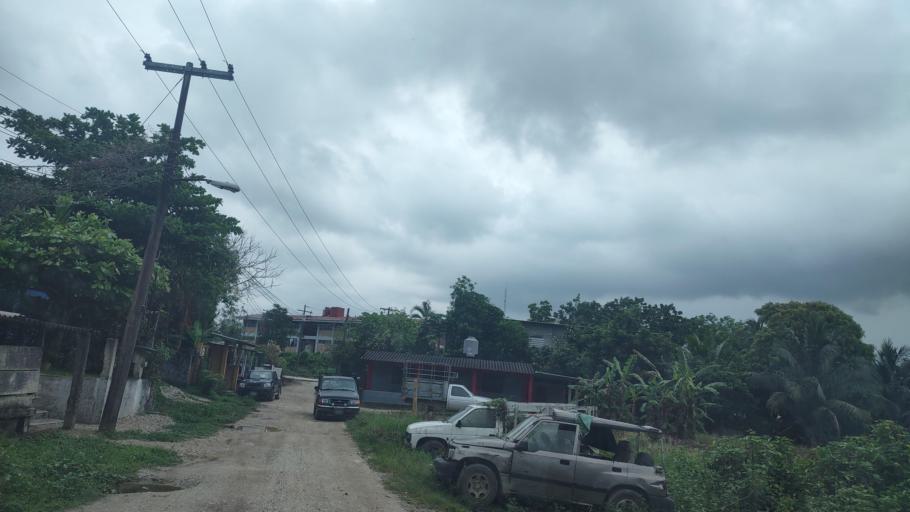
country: MX
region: Veracruz
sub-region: Uxpanapa
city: Poblado 10
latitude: 17.4980
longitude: -94.1615
